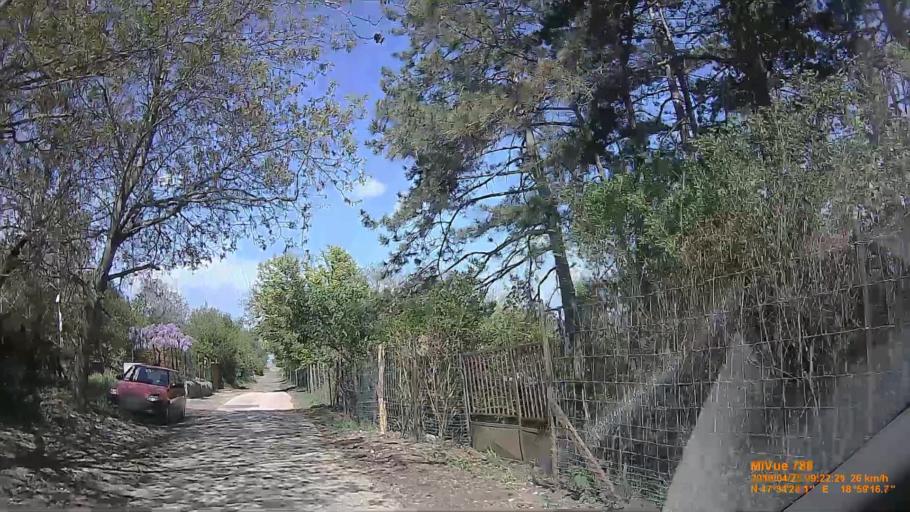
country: HU
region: Pest
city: Pilisborosjeno
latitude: 47.5726
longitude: 18.9879
